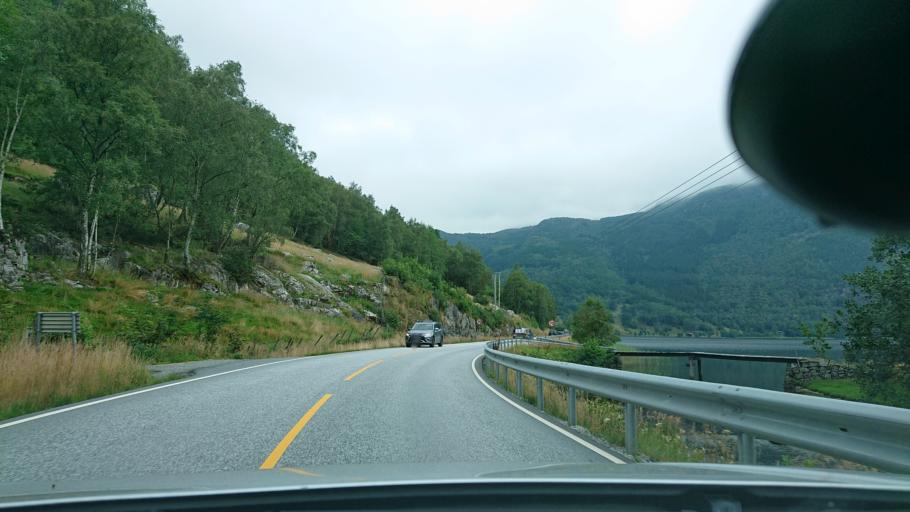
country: NO
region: Rogaland
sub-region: Hjelmeland
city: Hjelmelandsvagen
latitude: 59.1543
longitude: 6.1731
